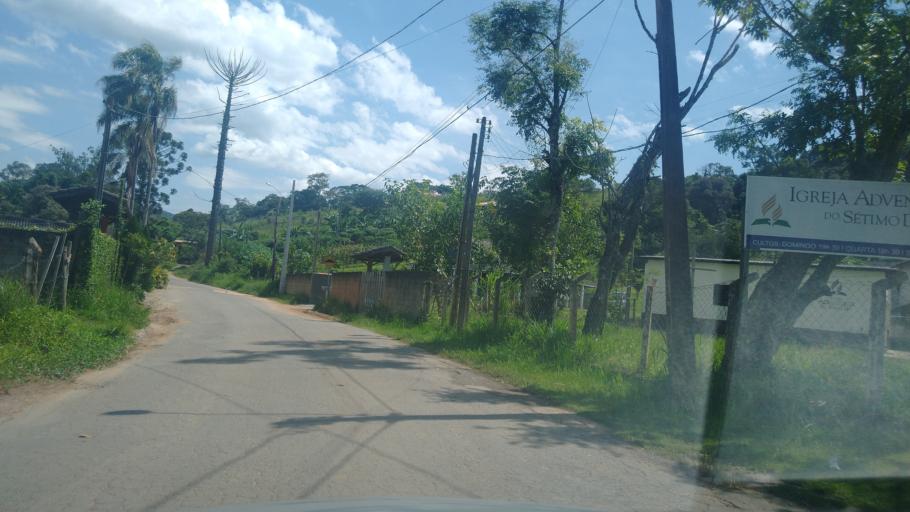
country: BR
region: Minas Gerais
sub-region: Extrema
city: Extrema
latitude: -22.7789
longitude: -46.2857
